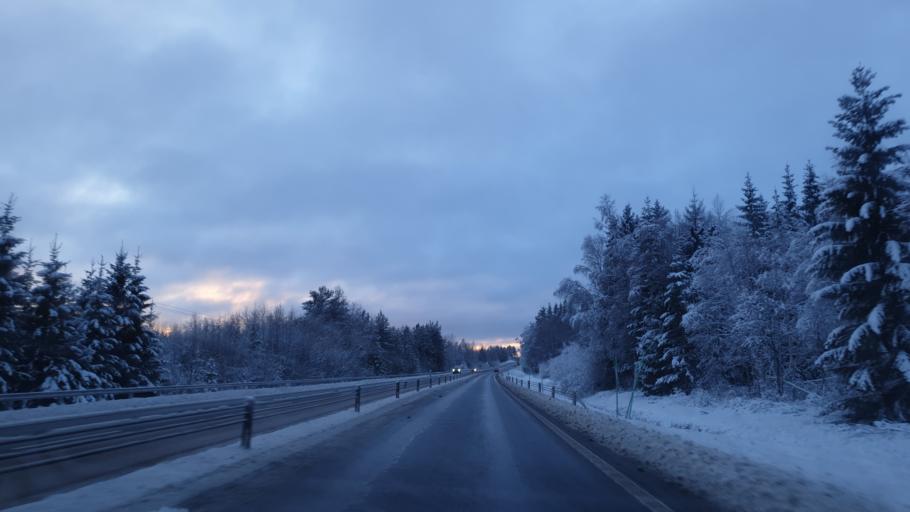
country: SE
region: Vaesterbotten
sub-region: Nordmalings Kommun
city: Nordmaling
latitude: 63.5247
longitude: 19.3851
